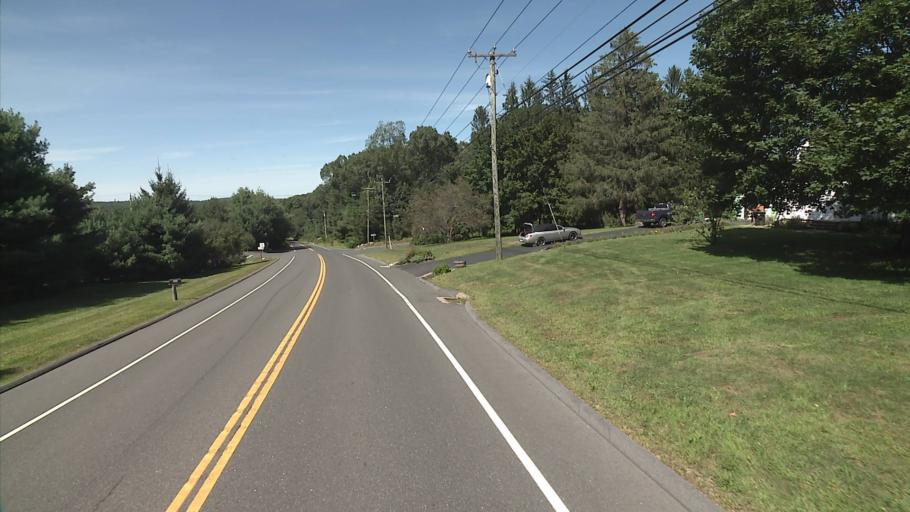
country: US
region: Connecticut
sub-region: New Haven County
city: Oxford
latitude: 41.4054
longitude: -73.1418
